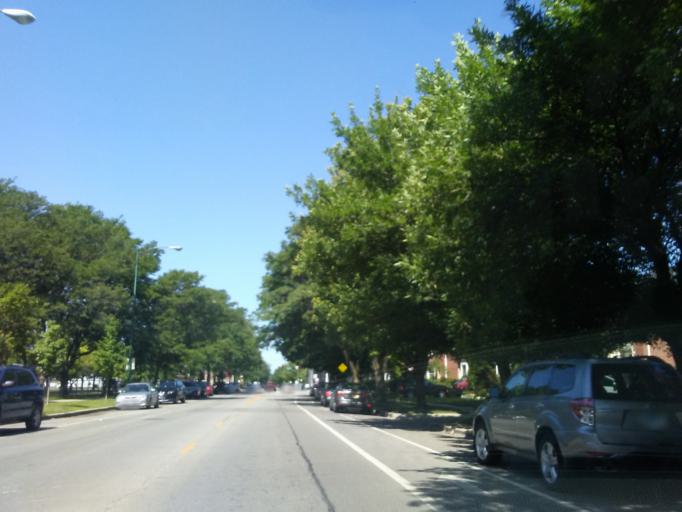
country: US
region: Illinois
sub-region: Cook County
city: Evanston
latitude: 42.0051
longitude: -87.6882
